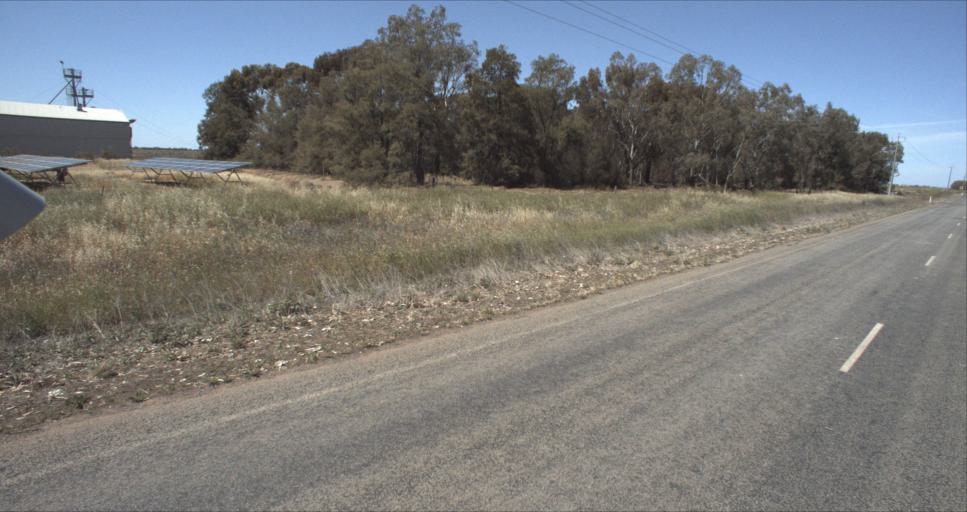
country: AU
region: New South Wales
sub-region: Leeton
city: Leeton
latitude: -34.4694
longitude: 146.2926
